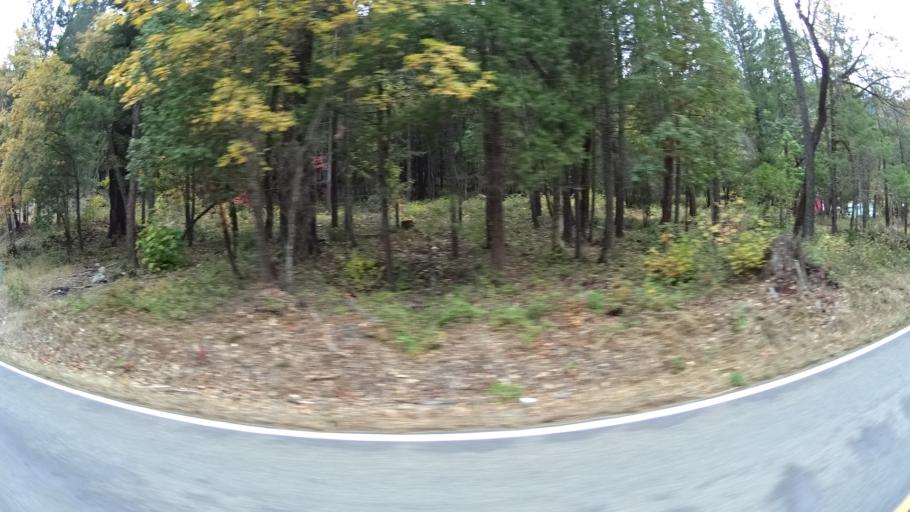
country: US
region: California
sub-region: Siskiyou County
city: Happy Camp
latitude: 41.8463
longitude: -123.3876
